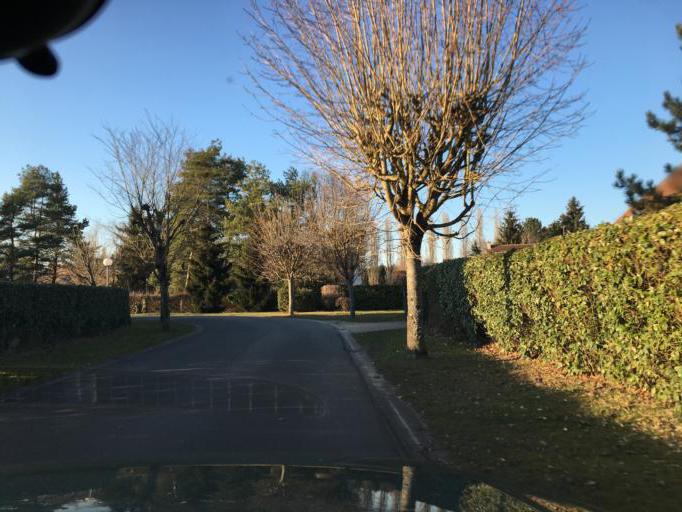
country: FR
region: Centre
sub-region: Departement du Loiret
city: Jouy-le-Potier
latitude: 47.7814
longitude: 1.8737
